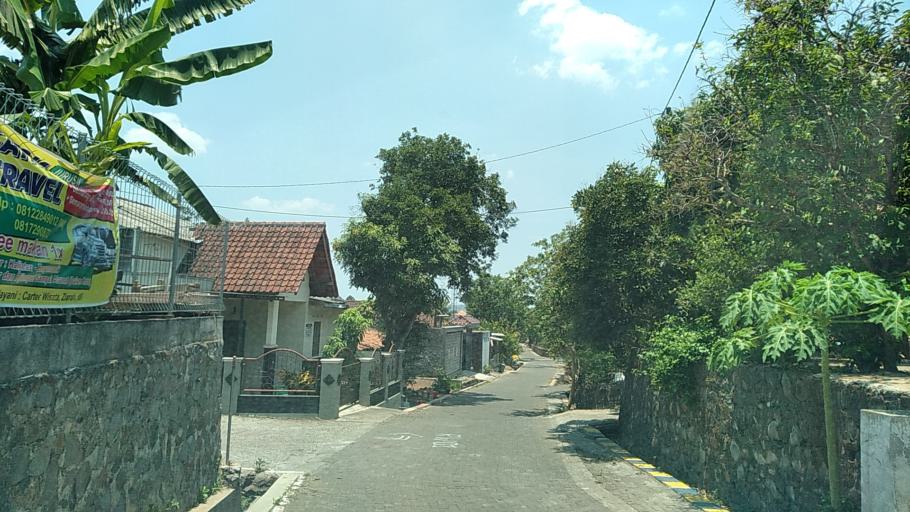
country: ID
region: Central Java
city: Ungaran
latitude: -7.0814
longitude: 110.4288
